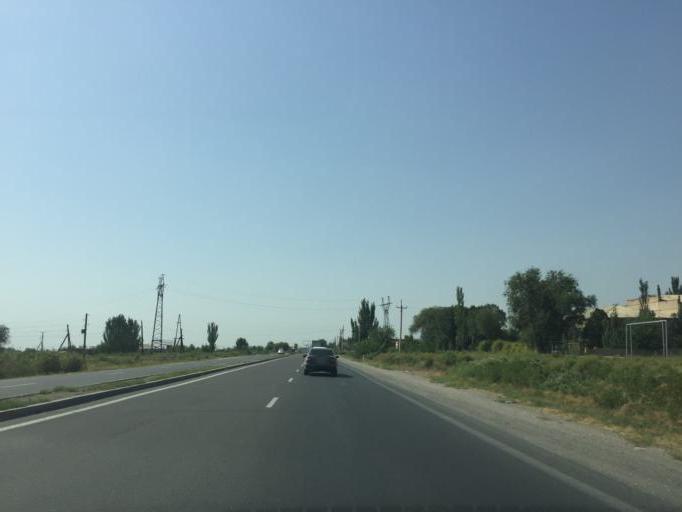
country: AM
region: Ararat
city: Shahumyan
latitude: 39.9397
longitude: 44.5576
